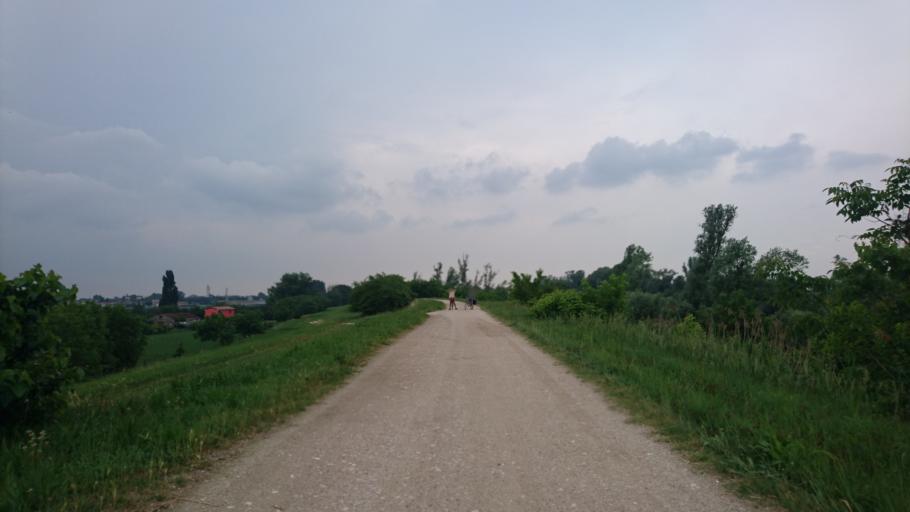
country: IT
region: Veneto
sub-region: Provincia di Padova
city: Masi
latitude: 45.1067
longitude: 11.5025
